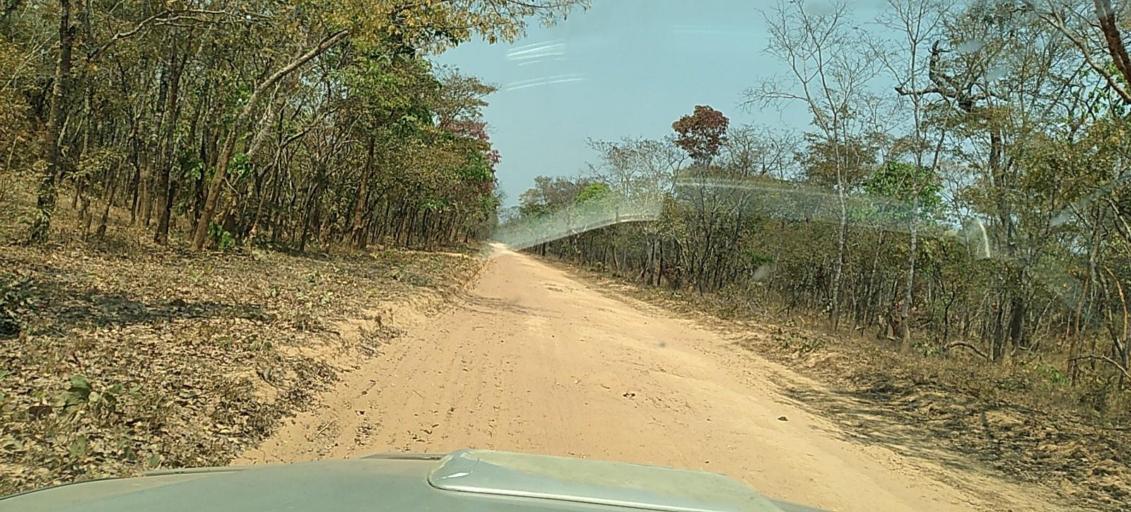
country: ZM
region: North-Western
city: Kasempa
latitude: -13.6566
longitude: 26.2614
